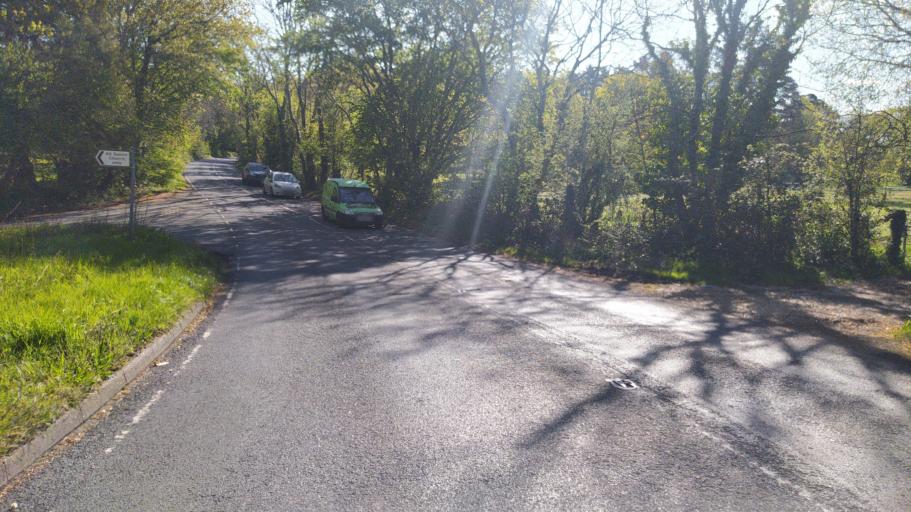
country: GB
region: England
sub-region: Hampshire
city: Marchwood
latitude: 50.8743
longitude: -1.4356
